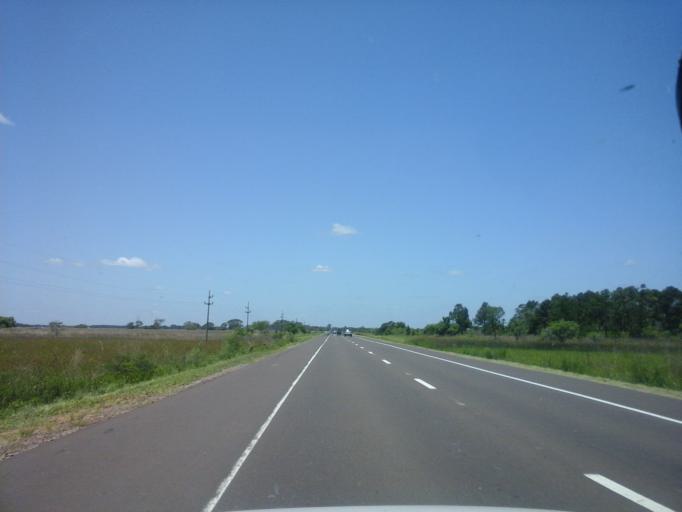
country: AR
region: Corrientes
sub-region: Departamento de San Cosme
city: San Cosme
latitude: -27.3709
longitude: -58.4785
